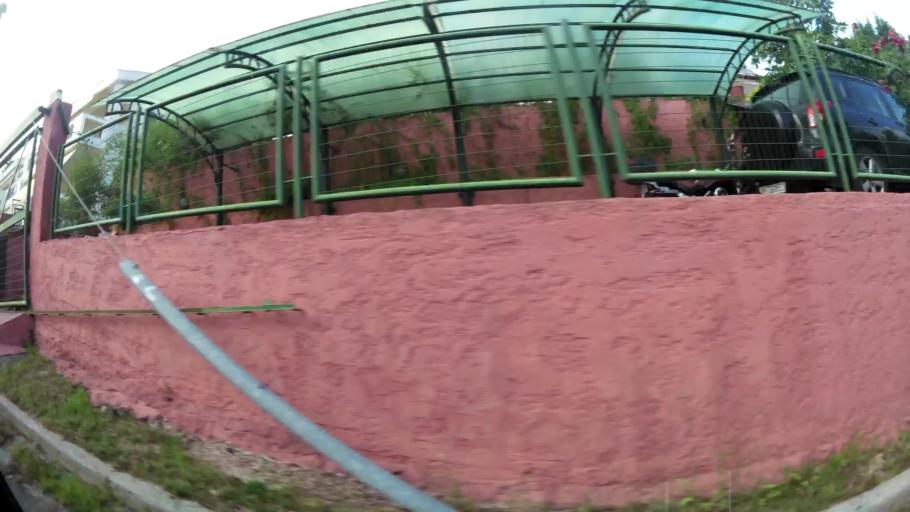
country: GR
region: Central Macedonia
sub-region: Nomos Thessalonikis
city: Pefka
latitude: 40.6603
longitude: 23.0009
